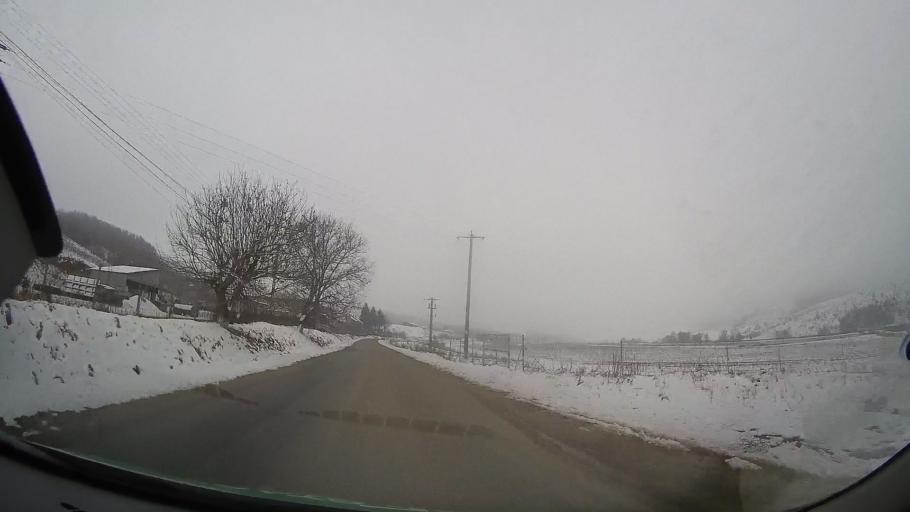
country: RO
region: Bacau
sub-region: Comuna Vultureni
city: Vultureni
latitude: 46.3682
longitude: 27.2833
